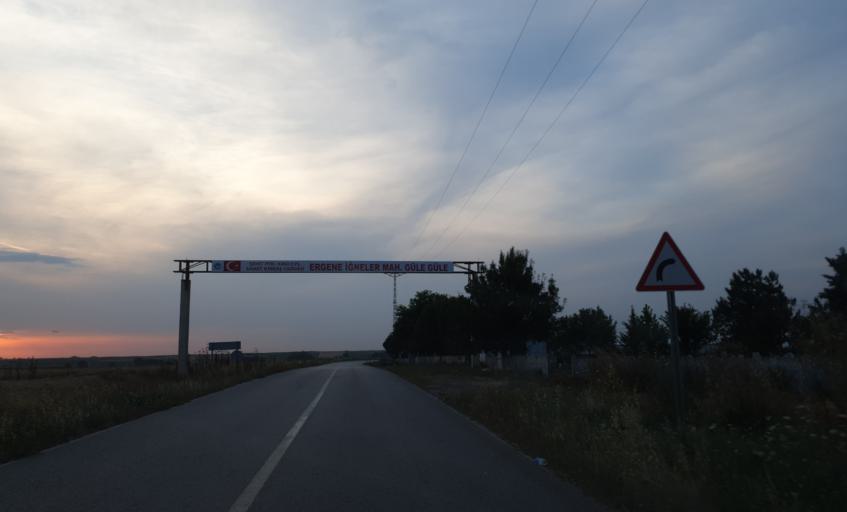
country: TR
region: Kirklareli
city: Buyukkaristiran
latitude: 41.3511
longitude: 27.6092
